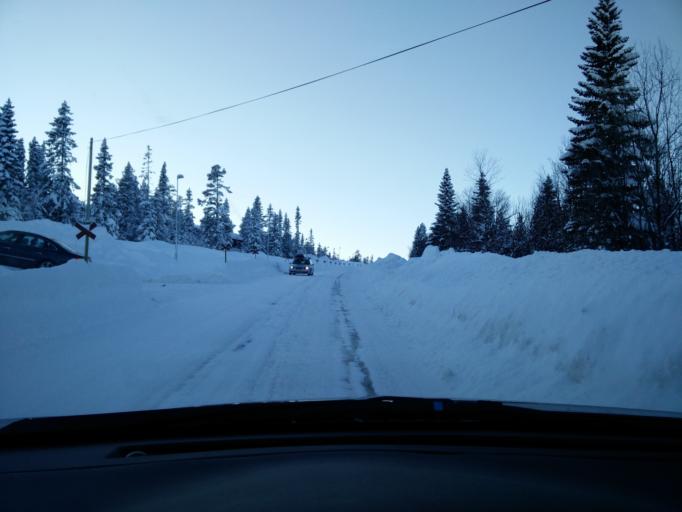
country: SE
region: Jaemtland
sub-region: Bergs Kommun
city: Hoverberg
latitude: 62.5018
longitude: 14.1058
